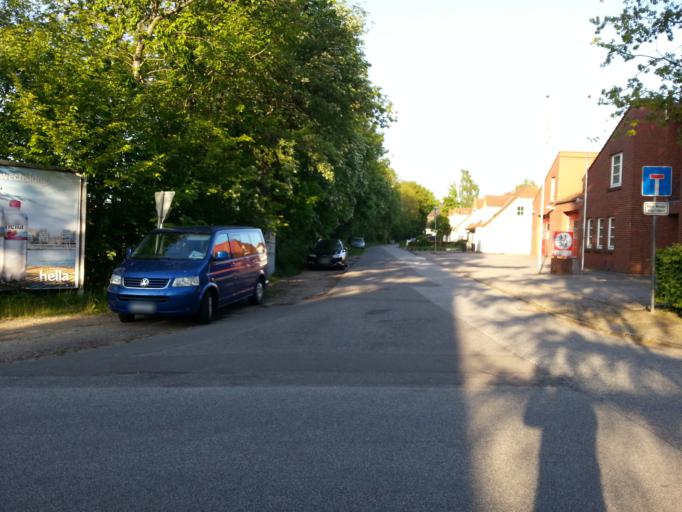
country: DE
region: Schleswig-Holstein
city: Travemuende
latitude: 53.9883
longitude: 10.8333
